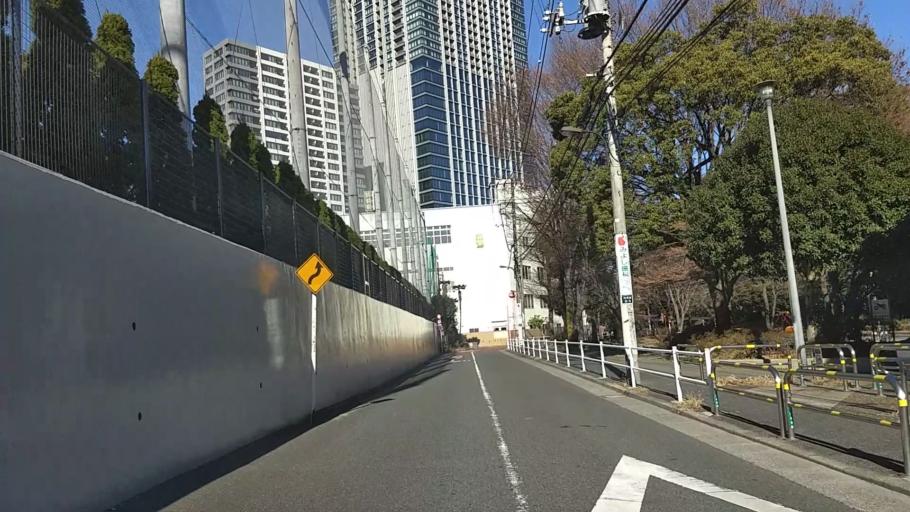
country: JP
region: Tokyo
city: Tokyo
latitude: 35.7051
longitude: 139.7034
